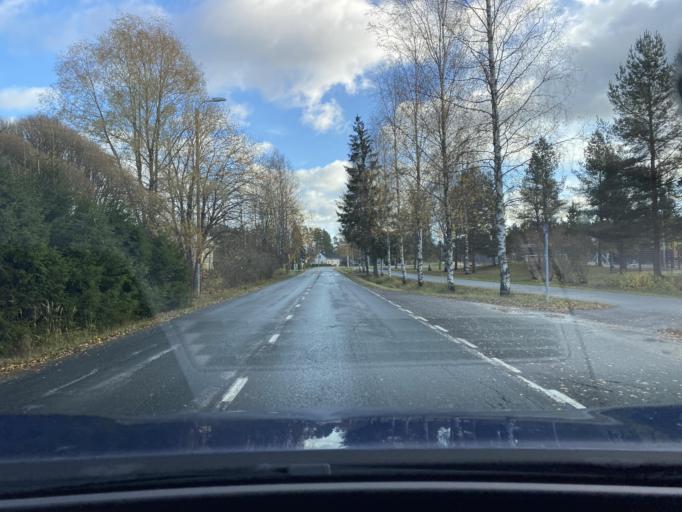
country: FI
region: Varsinais-Suomi
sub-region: Loimaa
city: Aura
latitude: 60.7224
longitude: 22.5960
